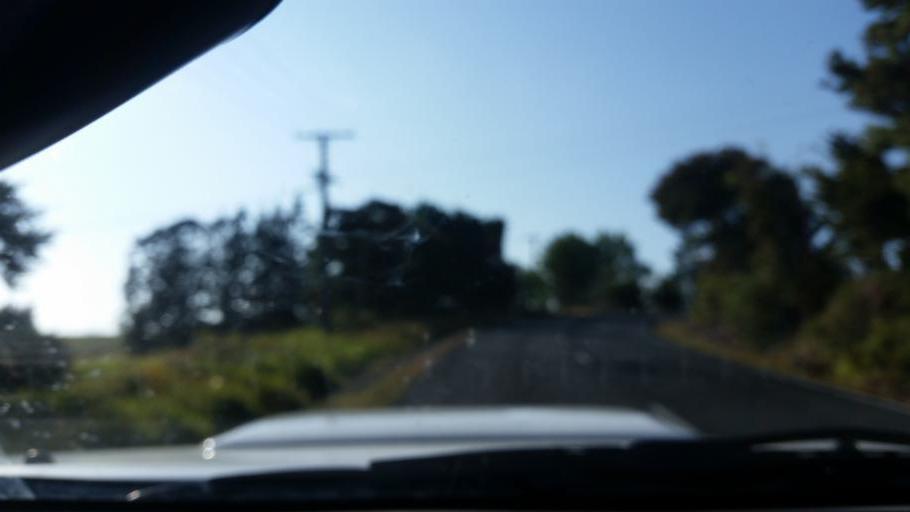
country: NZ
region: Northland
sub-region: Whangarei
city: Ruakaka
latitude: -36.1170
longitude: 174.2317
